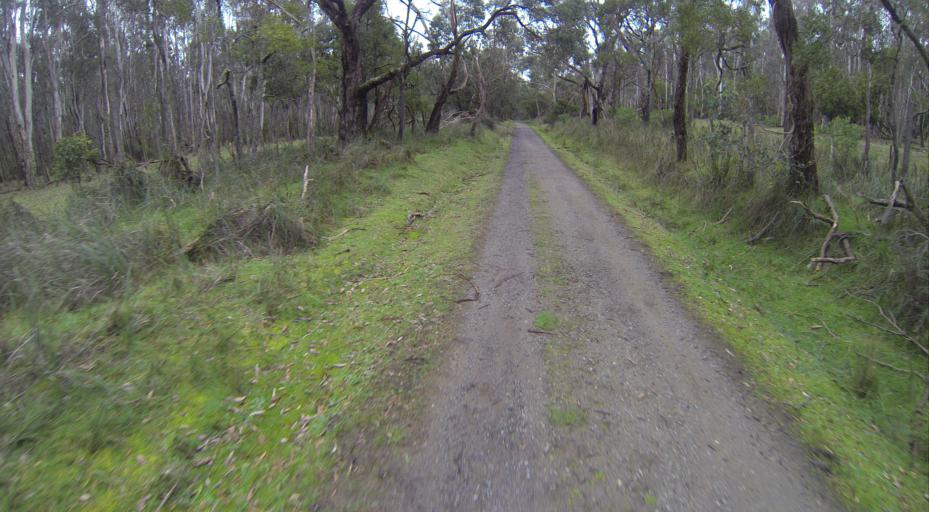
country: AU
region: Victoria
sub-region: Yarra Ranges
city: Lysterfield
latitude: -37.9457
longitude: 145.3096
